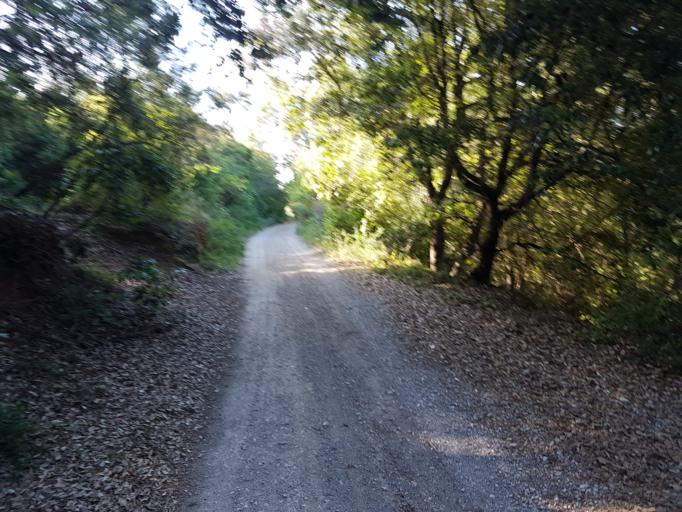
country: IT
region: Tuscany
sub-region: Provincia di Livorno
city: Capoliveri
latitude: 42.7840
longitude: 10.3511
